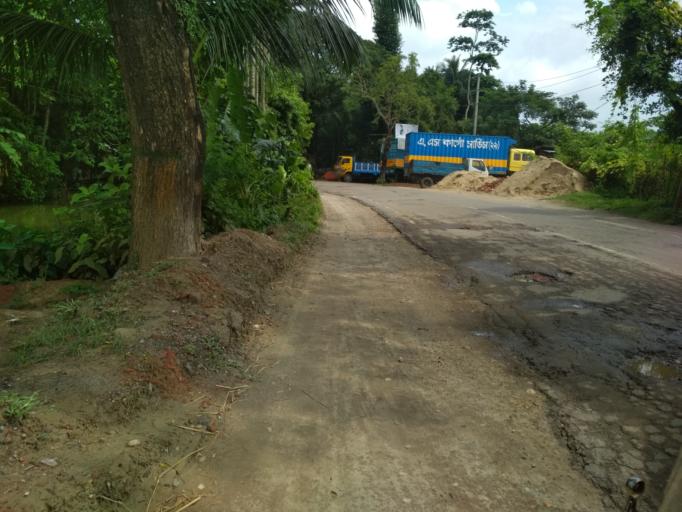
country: BD
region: Chittagong
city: Lakshmipur
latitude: 22.9674
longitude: 90.8098
